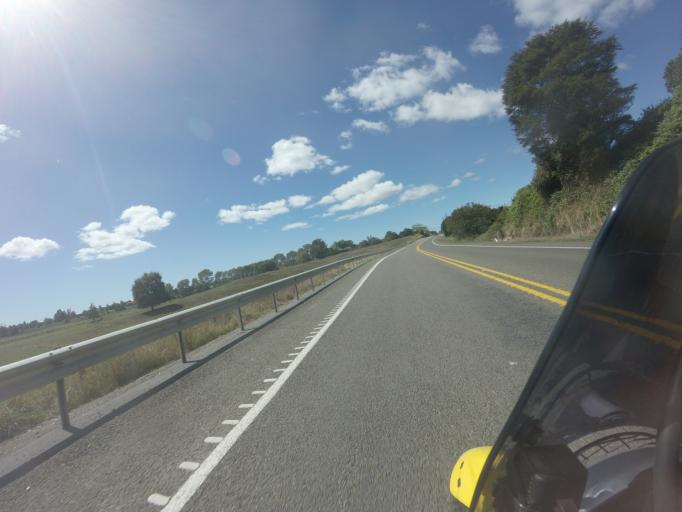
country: NZ
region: Bay of Plenty
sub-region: Whakatane District
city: Edgecumbe
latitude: -37.9988
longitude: 176.8726
